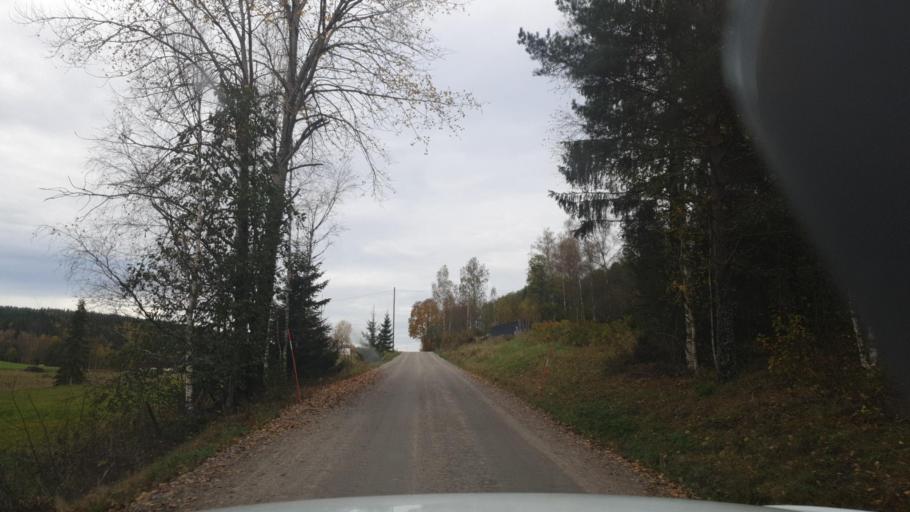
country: SE
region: Vaermland
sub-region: Arvika Kommun
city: Arvika
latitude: 59.6853
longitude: 12.7728
